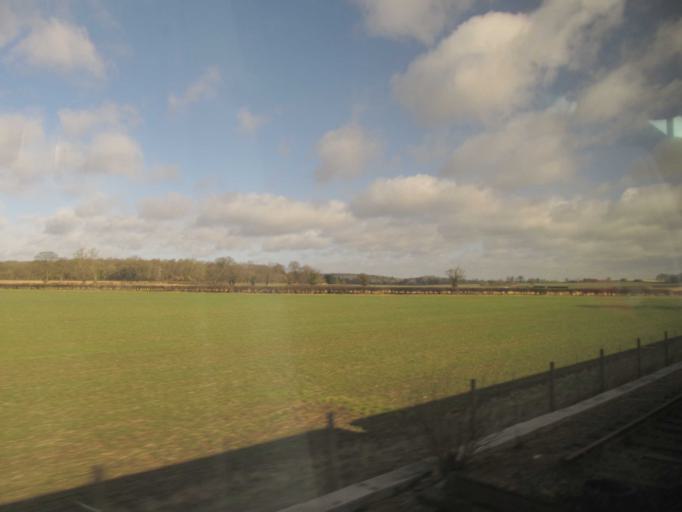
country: GB
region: England
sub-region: Wokingham
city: Twyford
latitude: 51.4855
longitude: -0.8325
